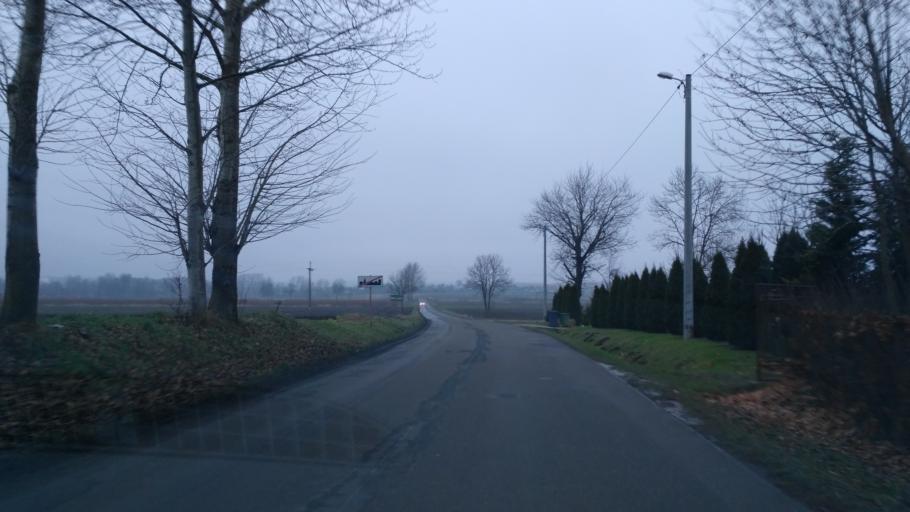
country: PL
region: Subcarpathian Voivodeship
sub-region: Powiat przeworski
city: Zarzecze
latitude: 49.9760
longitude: 22.5530
